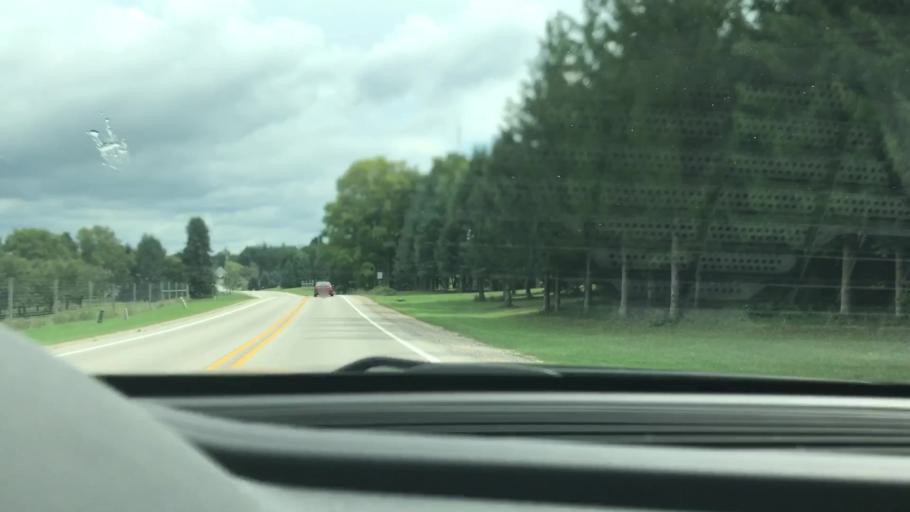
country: US
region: Michigan
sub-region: Antrim County
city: Bellaire
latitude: 45.0980
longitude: -85.3013
